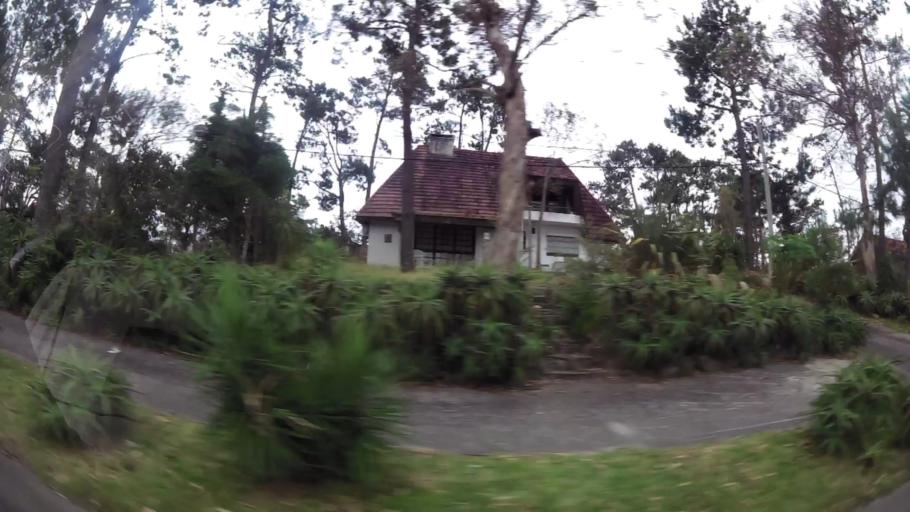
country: UY
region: Maldonado
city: Maldonado
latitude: -34.9065
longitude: -55.0005
